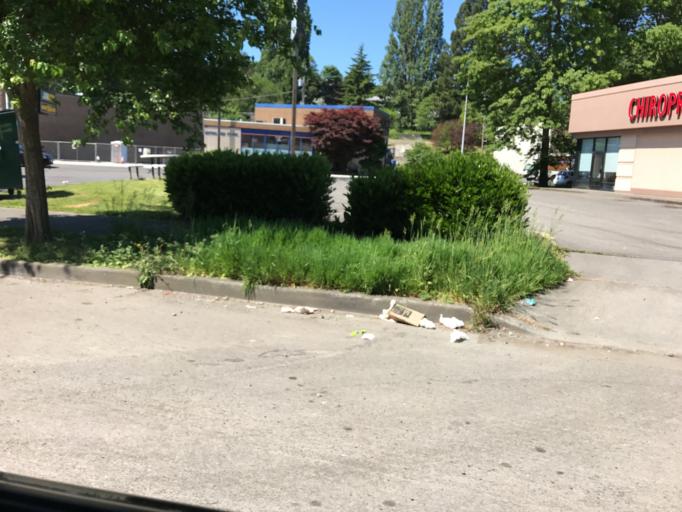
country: US
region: Washington
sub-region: King County
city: Seattle
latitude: 47.5822
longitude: -122.3004
